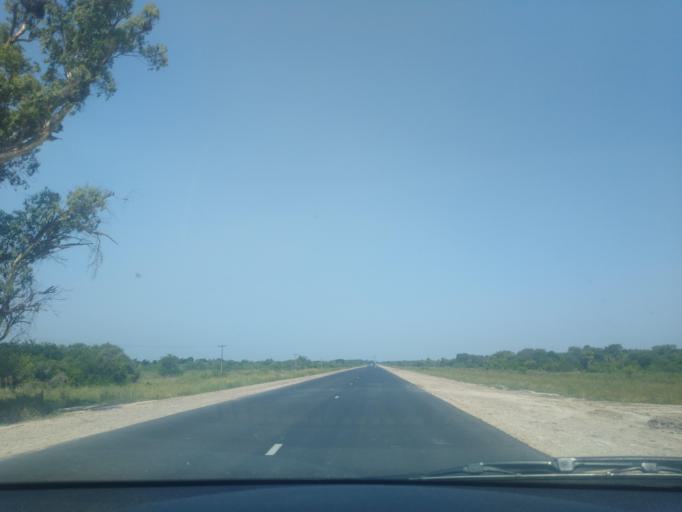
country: AR
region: Chaco
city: Puerto Tirol
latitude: -27.5695
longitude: -59.2730
